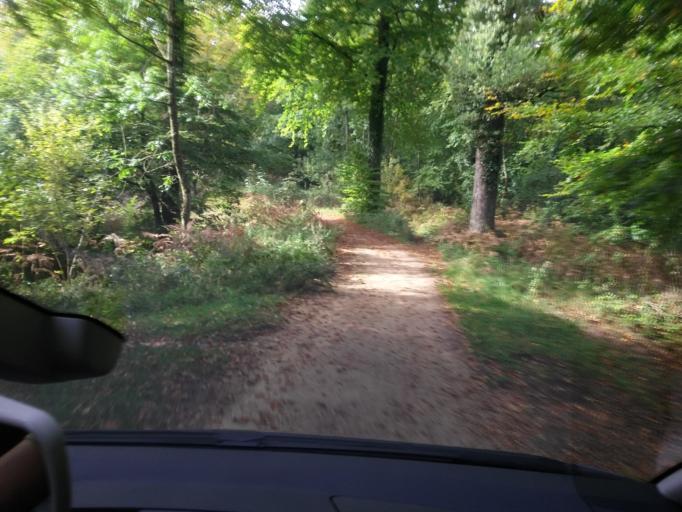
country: BE
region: Wallonia
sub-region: Province du Luxembourg
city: Attert
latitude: 49.7165
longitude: 5.7871
